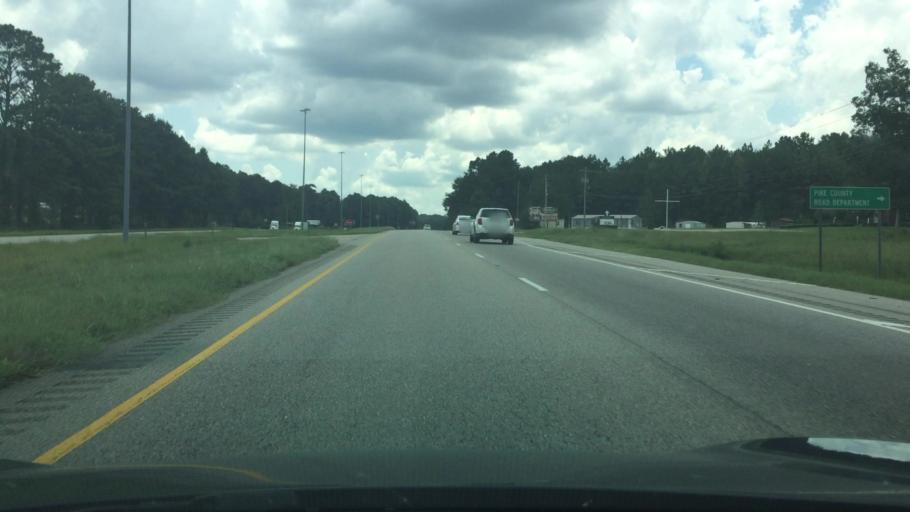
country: US
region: Alabama
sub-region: Pike County
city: Troy
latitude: 31.8402
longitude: -85.9936
